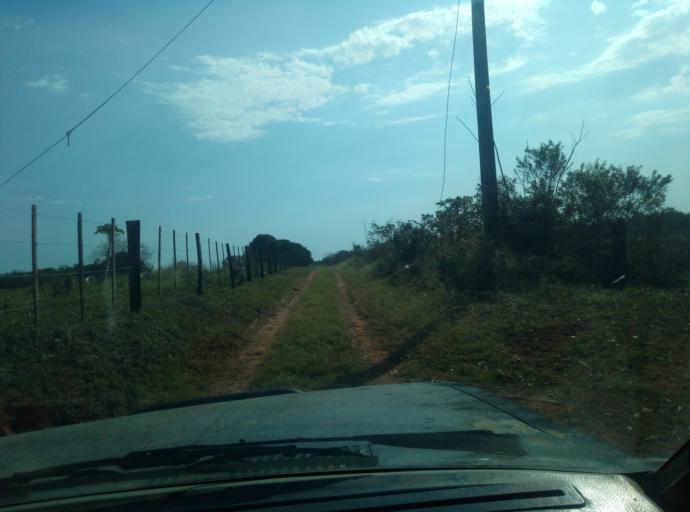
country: PY
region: Caaguazu
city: Doctor Cecilio Baez
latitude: -25.1419
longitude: -56.2565
